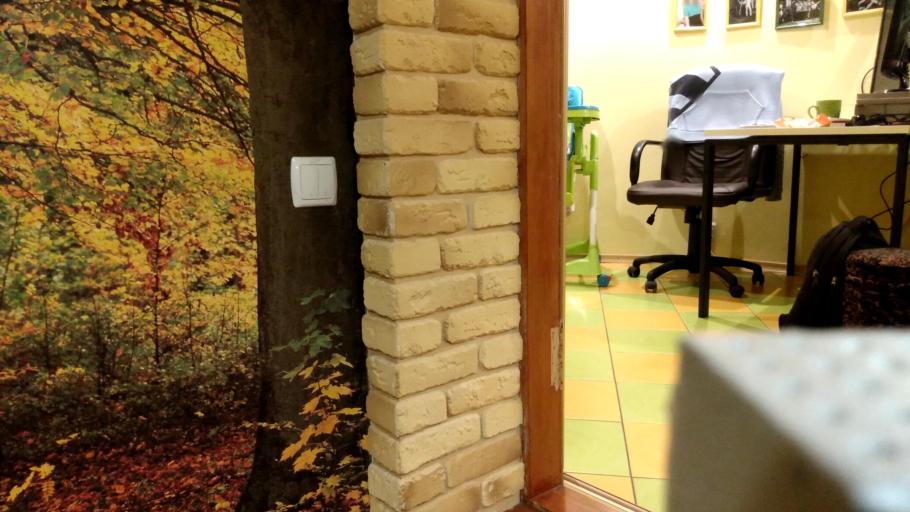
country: RU
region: Republic of Karelia
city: Pudozh
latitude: 61.8118
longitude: 37.6675
